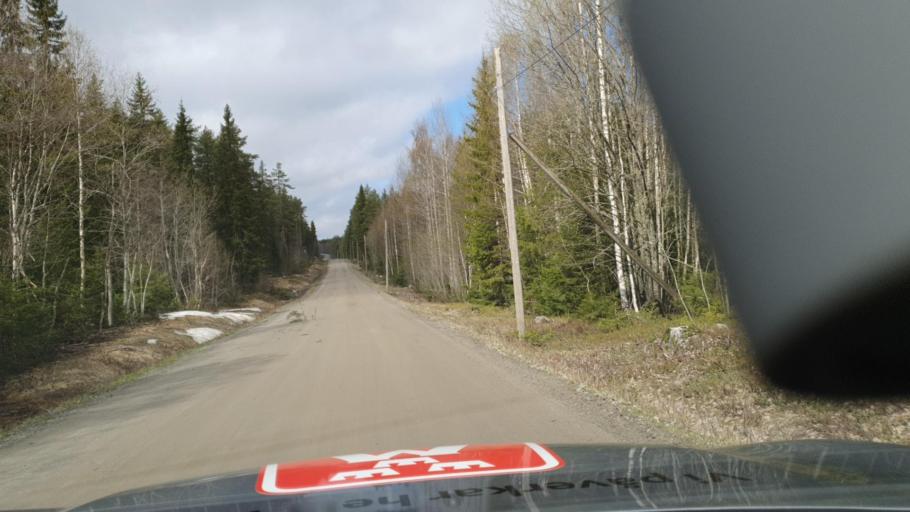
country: SE
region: Vaesterbotten
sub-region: Bjurholms Kommun
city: Bjurholm
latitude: 63.6755
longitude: 18.9936
